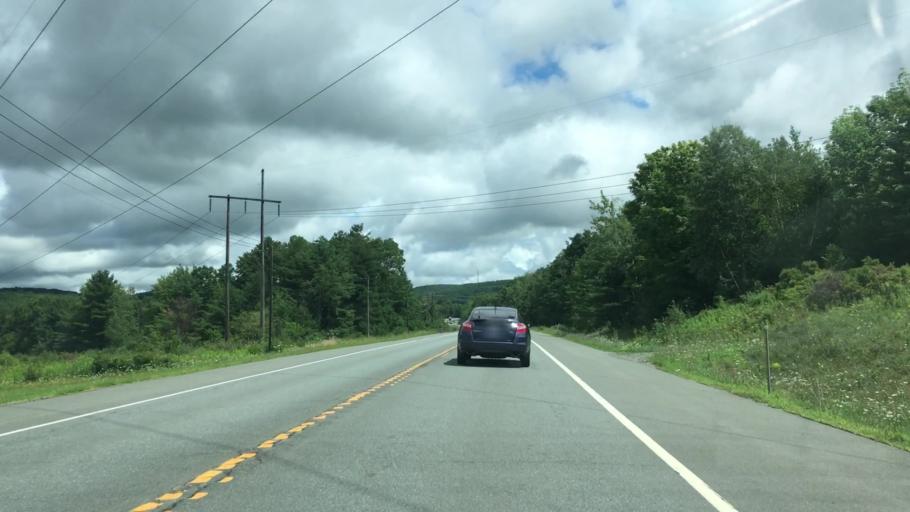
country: US
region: New York
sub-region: Rensselaer County
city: Hoosick Falls
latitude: 42.8485
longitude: -73.4401
